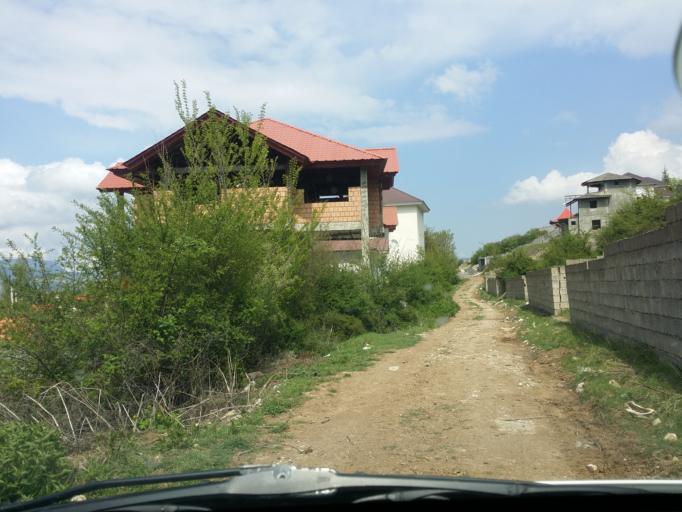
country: IR
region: Mazandaran
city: `Abbasabad
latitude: 36.4965
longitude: 51.1516
